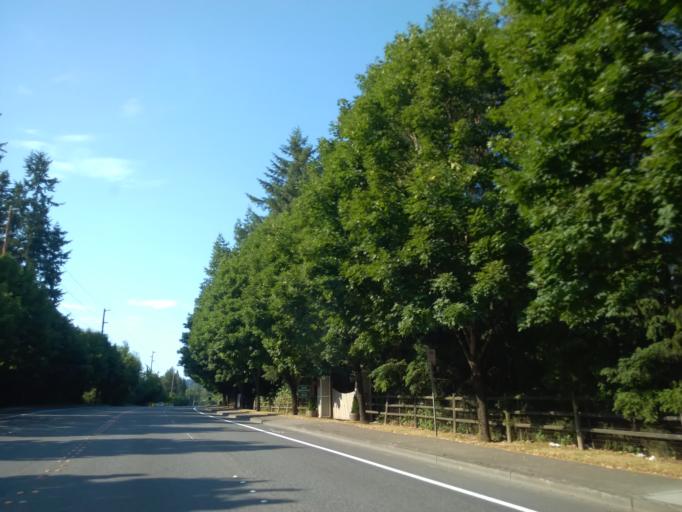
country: US
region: Washington
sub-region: King County
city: Redmond
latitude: 47.6959
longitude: -122.0932
